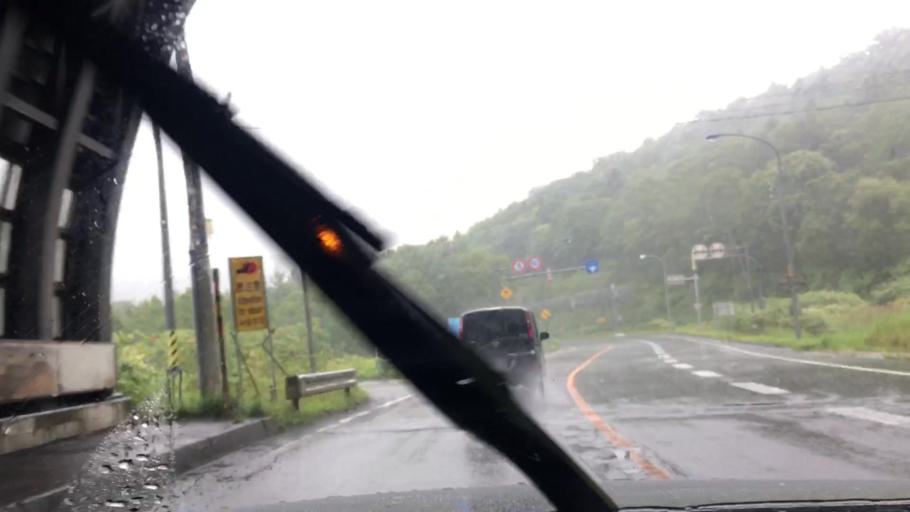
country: JP
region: Hokkaido
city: Sapporo
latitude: 42.8482
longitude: 141.0792
